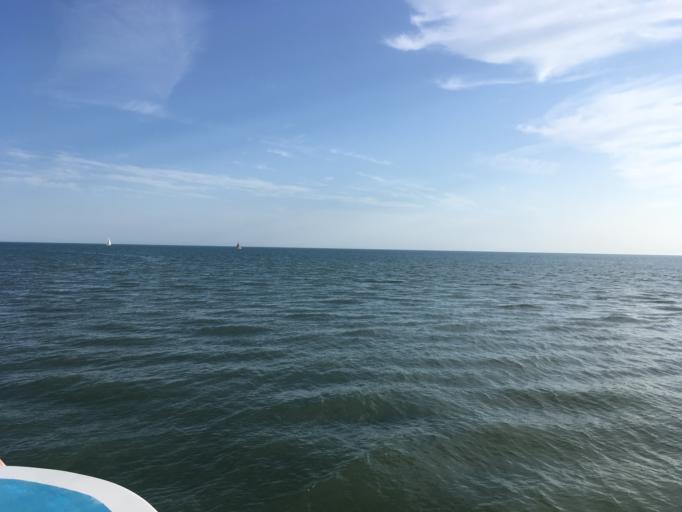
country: FR
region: Provence-Alpes-Cote d'Azur
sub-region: Departement des Bouches-du-Rhone
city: Saintes-Maries-de-la-Mer
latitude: 43.4498
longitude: 4.3976
